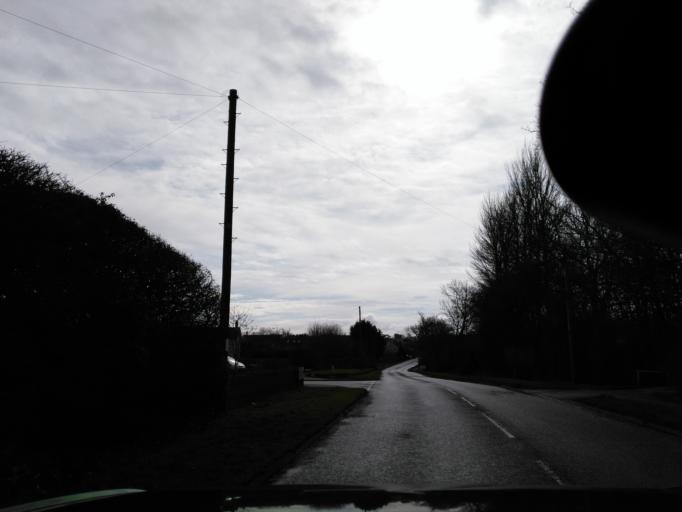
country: GB
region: England
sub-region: Wiltshire
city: Corsham
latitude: 51.4233
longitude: -2.1811
